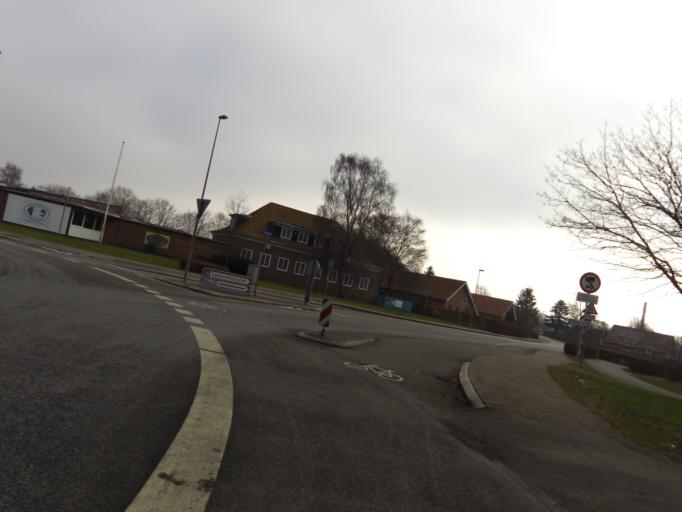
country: DK
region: South Denmark
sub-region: Tonder Kommune
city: Logumkloster
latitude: 55.0636
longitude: 8.9553
